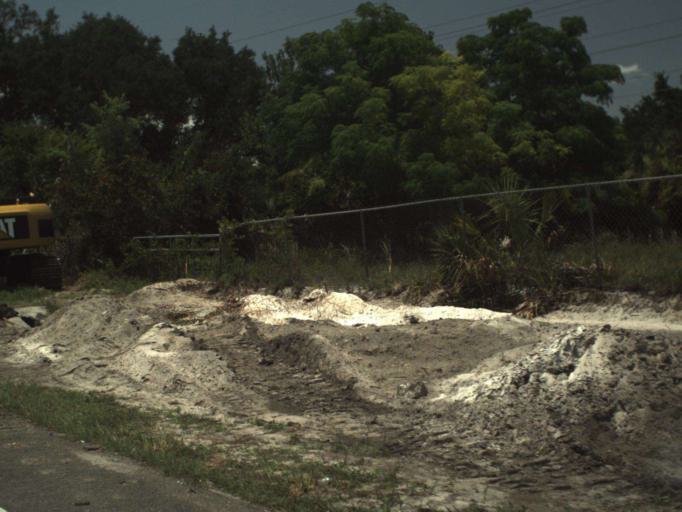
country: US
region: Florida
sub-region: Seminole County
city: Winter Springs
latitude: 28.7041
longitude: -81.2930
